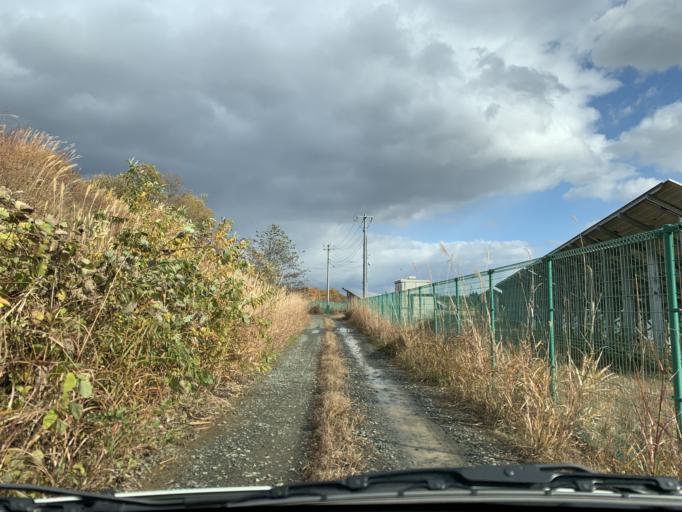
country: JP
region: Iwate
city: Mizusawa
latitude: 39.1123
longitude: 140.9543
